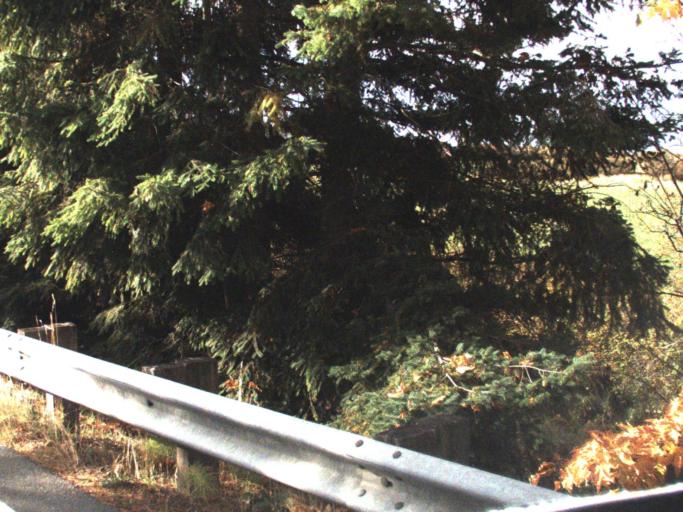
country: US
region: Washington
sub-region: Whatcom County
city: Sudden Valley
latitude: 48.5974
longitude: -122.4220
